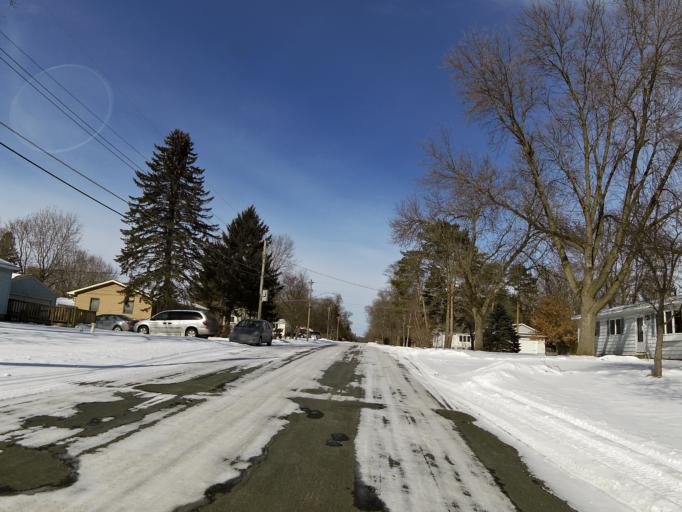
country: US
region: Minnesota
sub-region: Washington County
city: Lake Saint Croix Beach
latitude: 44.9221
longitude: -92.7687
